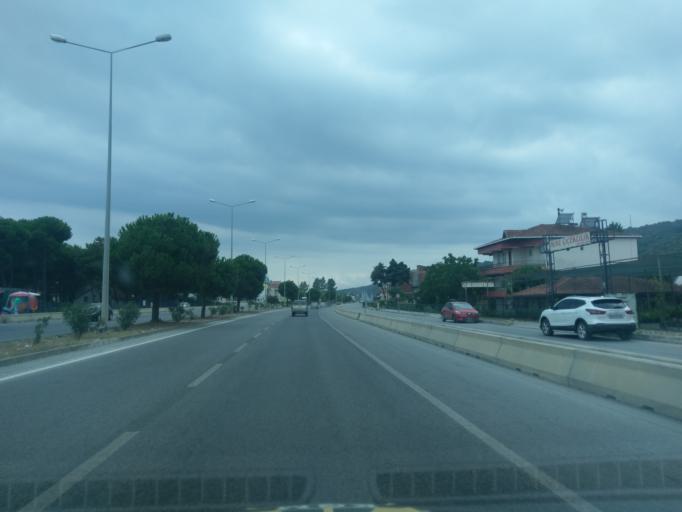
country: TR
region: Samsun
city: Taflan
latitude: 41.3963
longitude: 36.1971
